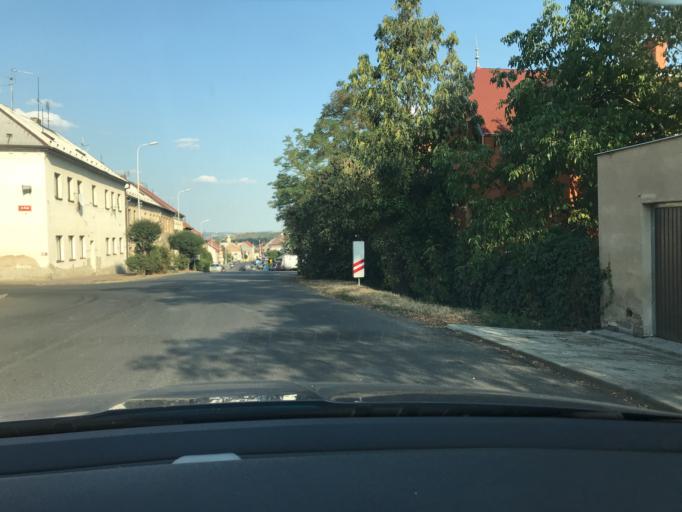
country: CZ
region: Ustecky
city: Postoloprty
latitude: 50.3615
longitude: 13.6910
